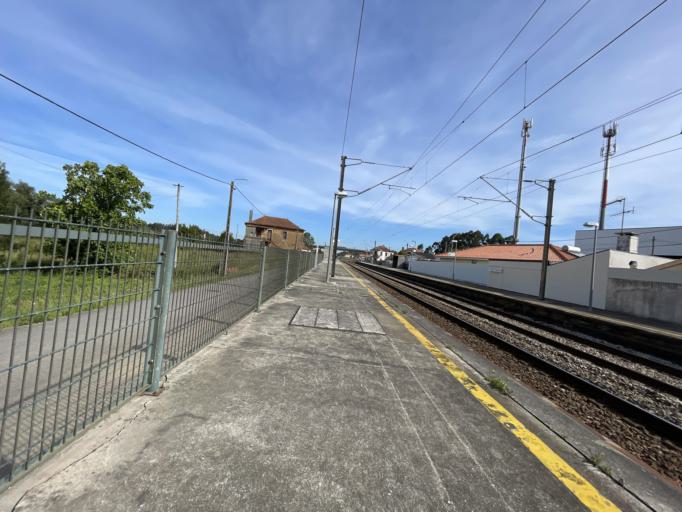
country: PT
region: Aveiro
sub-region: Ovar
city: Cortegaca
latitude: 40.9402
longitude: -8.6301
